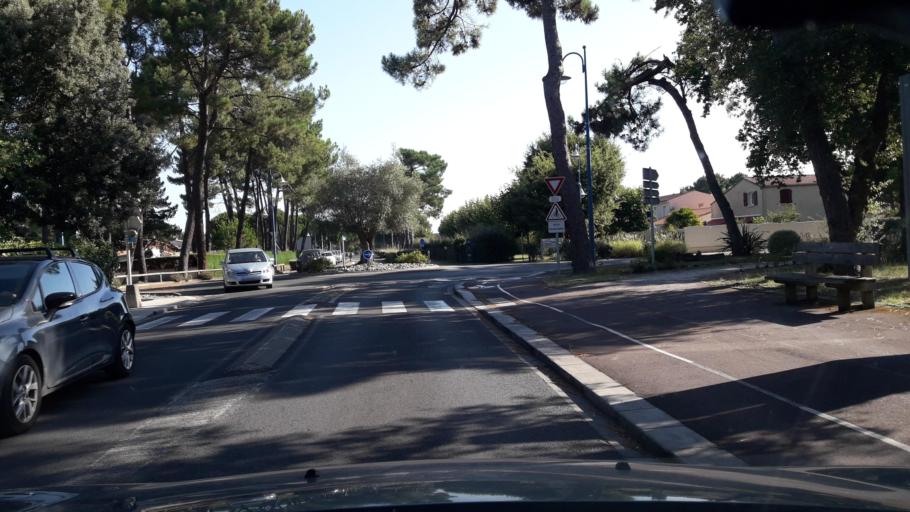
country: FR
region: Poitou-Charentes
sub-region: Departement de la Charente-Maritime
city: Les Mathes
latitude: 45.6938
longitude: -1.1778
